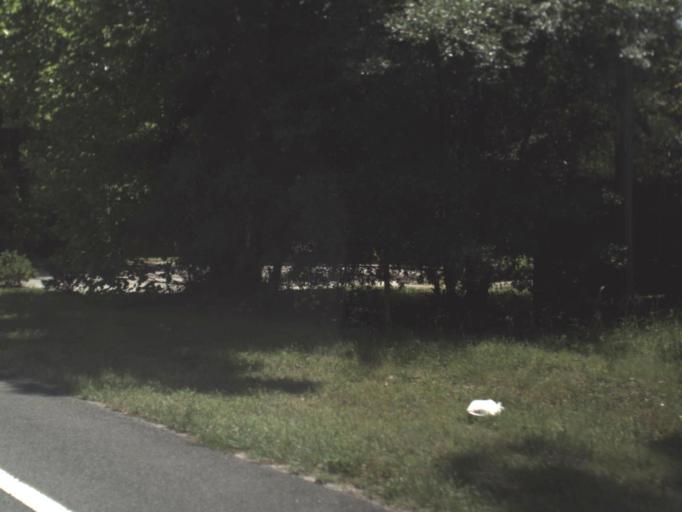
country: US
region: Florida
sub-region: Nassau County
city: Yulee
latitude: 30.5345
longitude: -81.6215
